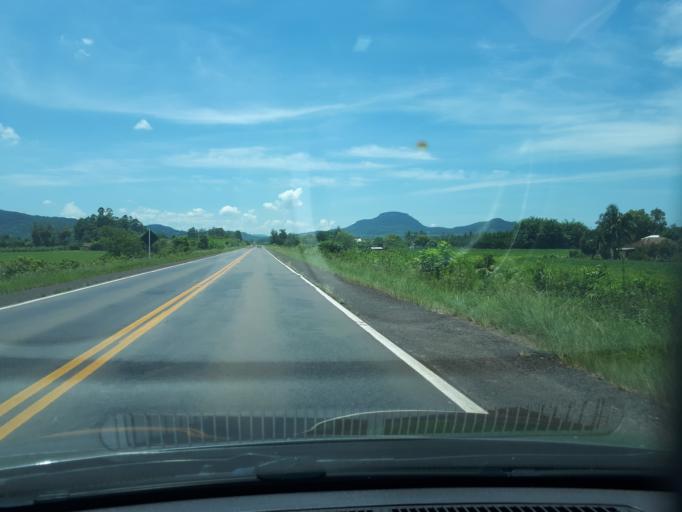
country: BR
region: Rio Grande do Sul
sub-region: Candelaria
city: Candelaria
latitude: -29.7241
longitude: -52.9210
